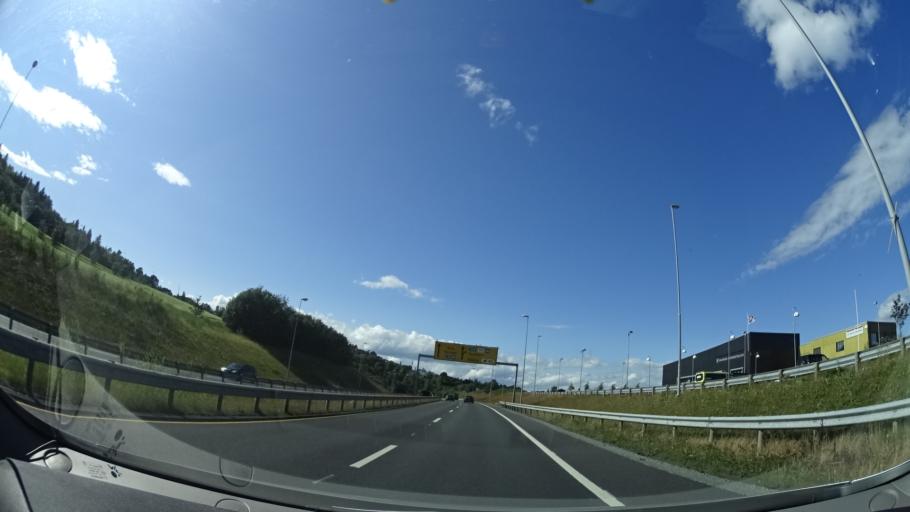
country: NO
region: Sor-Trondelag
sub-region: Trondheim
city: Trondheim
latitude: 63.4259
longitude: 10.5157
